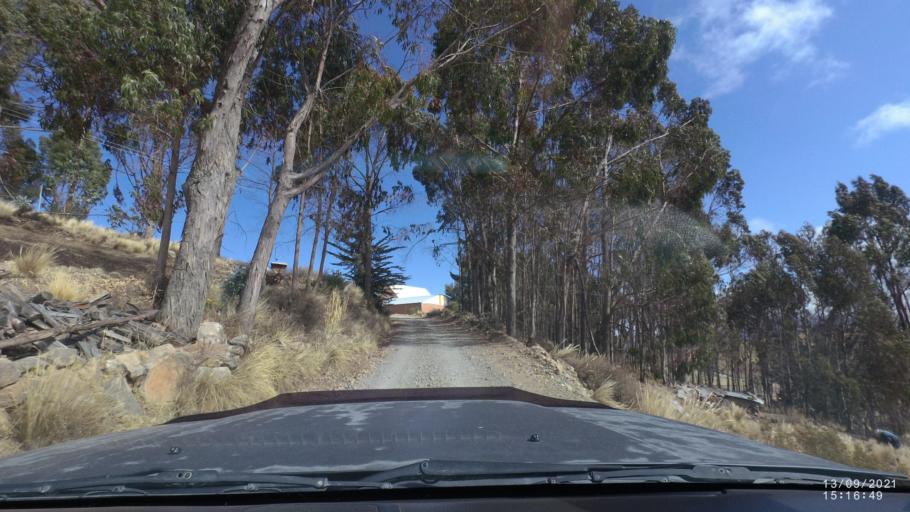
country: BO
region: Cochabamba
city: Colomi
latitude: -17.3673
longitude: -65.7912
